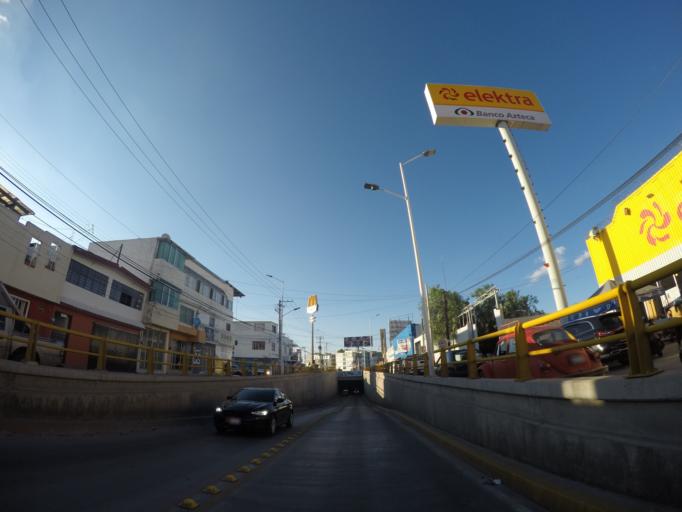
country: MX
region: San Luis Potosi
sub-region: San Luis Potosi
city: San Luis Potosi
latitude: 22.1689
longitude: -101.0018
